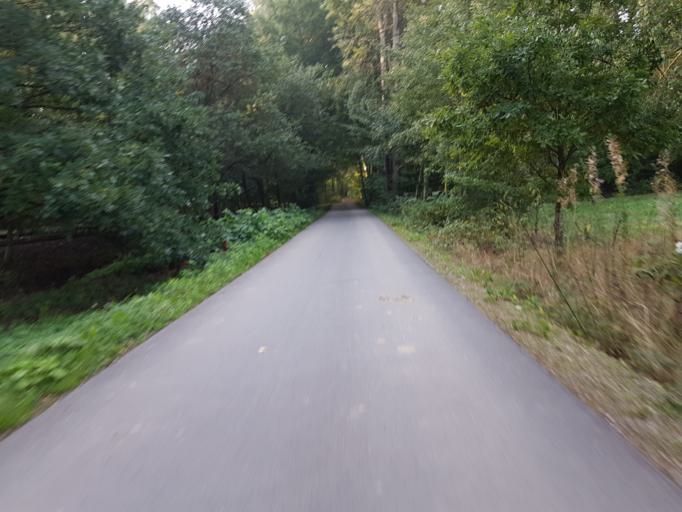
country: DE
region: Saxony
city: Claussnitz
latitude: 50.9112
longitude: 12.8963
